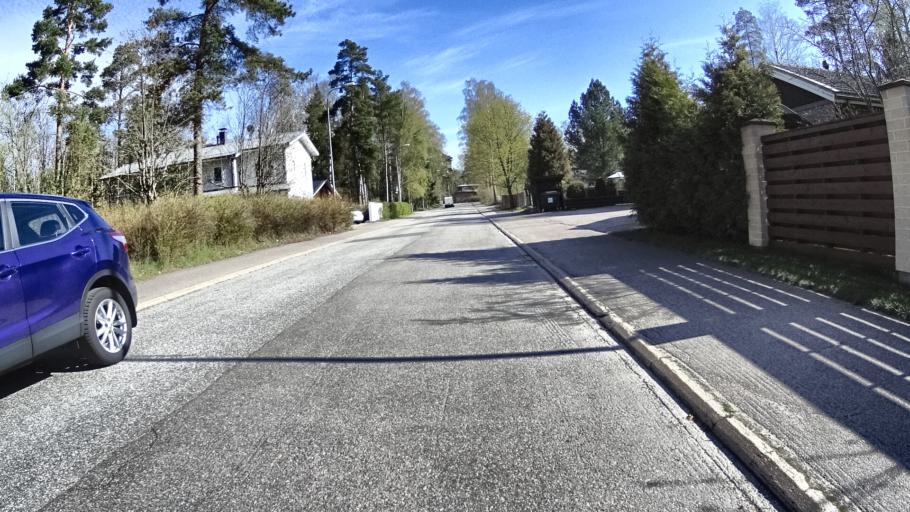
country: FI
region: Uusimaa
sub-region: Helsinki
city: Vantaa
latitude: 60.2268
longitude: 25.0582
